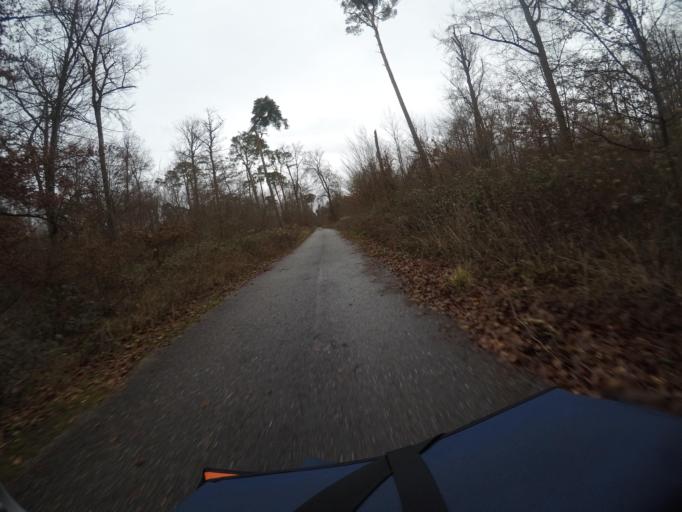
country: DE
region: Baden-Wuerttemberg
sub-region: Karlsruhe Region
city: Philippsburg
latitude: 49.2195
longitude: 8.4789
